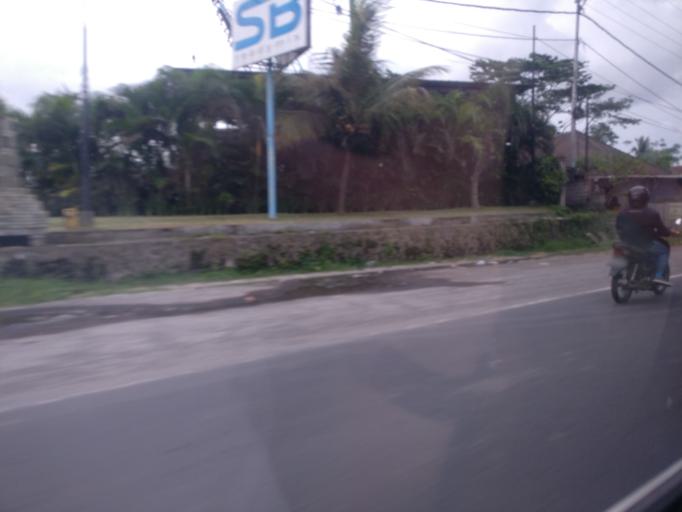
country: ID
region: Bali
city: Banjar Pasekan
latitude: -8.5969
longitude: 115.3314
